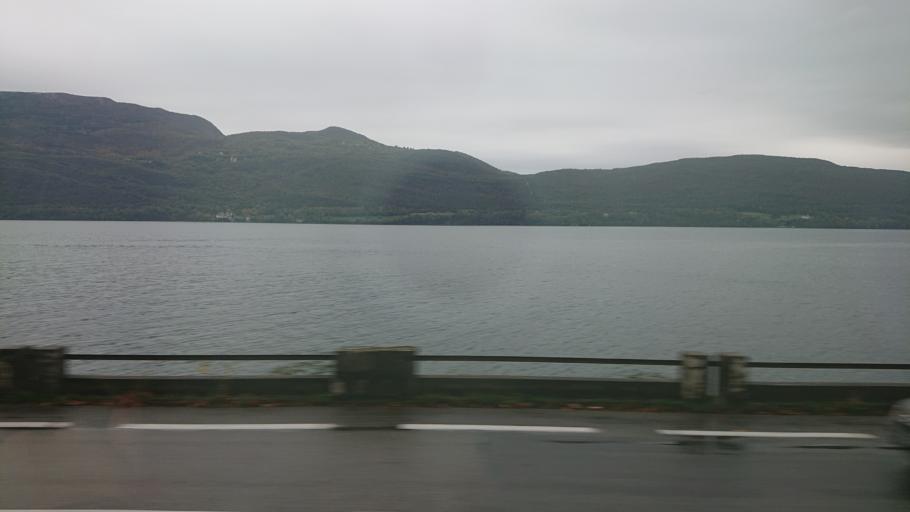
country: FR
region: Rhone-Alpes
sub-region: Departement de la Savoie
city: Chatillon
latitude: 45.7691
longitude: 5.8696
